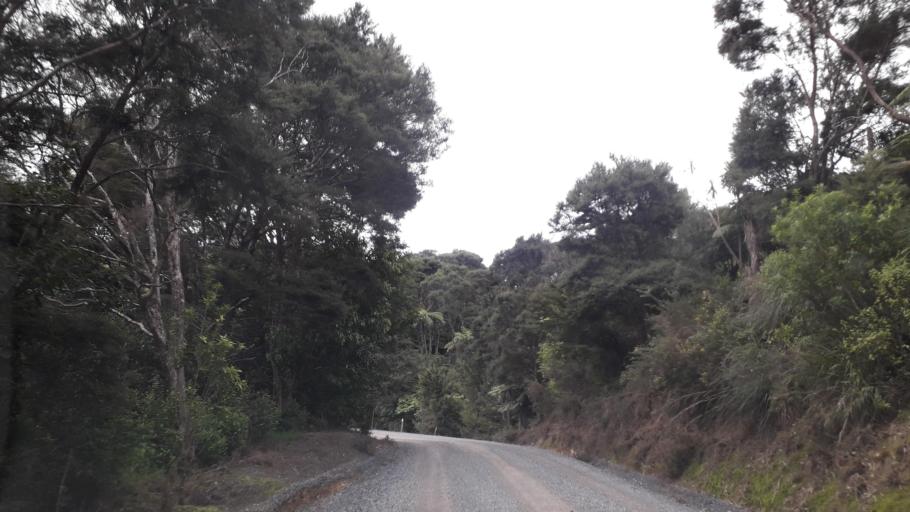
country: NZ
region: Northland
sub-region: Far North District
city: Paihia
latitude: -35.3182
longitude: 174.2314
